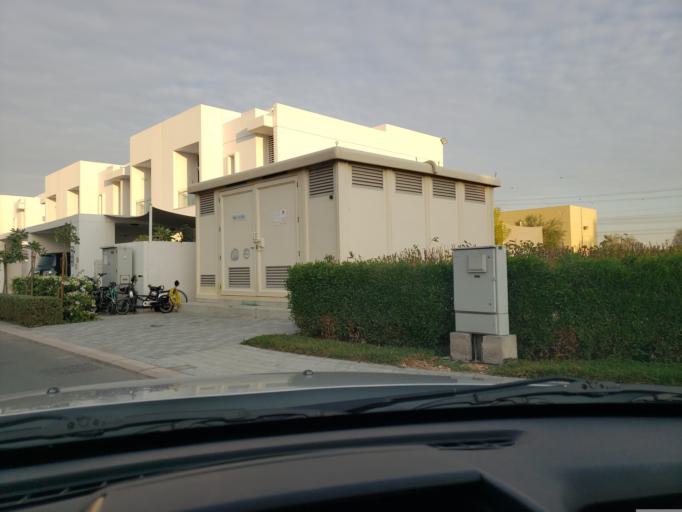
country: AE
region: Dubai
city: Dubai
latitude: 25.0144
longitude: 55.2710
